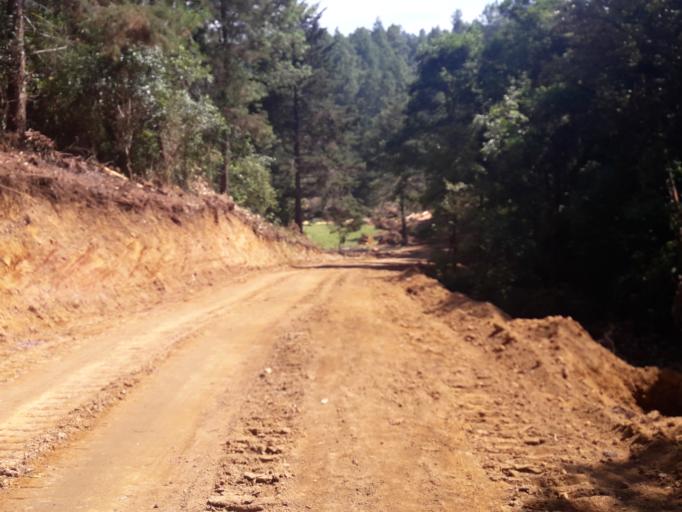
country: GT
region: Quiche
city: Nebaj
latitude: 15.4267
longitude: -91.1364
